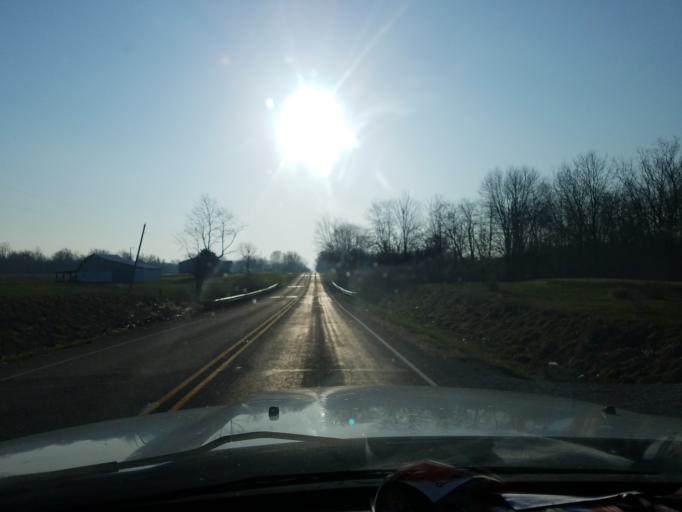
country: US
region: Indiana
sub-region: Clay County
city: Middlebury
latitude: 39.3884
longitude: -87.1768
